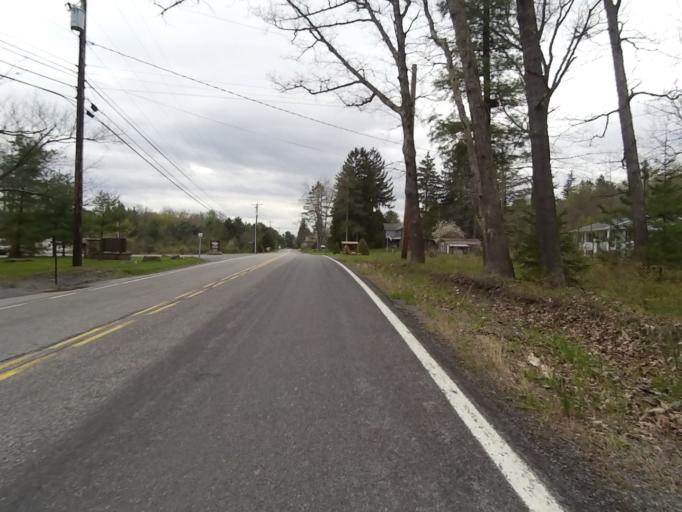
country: US
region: Pennsylvania
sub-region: Centre County
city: Stormstown
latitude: 40.9141
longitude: -78.0675
